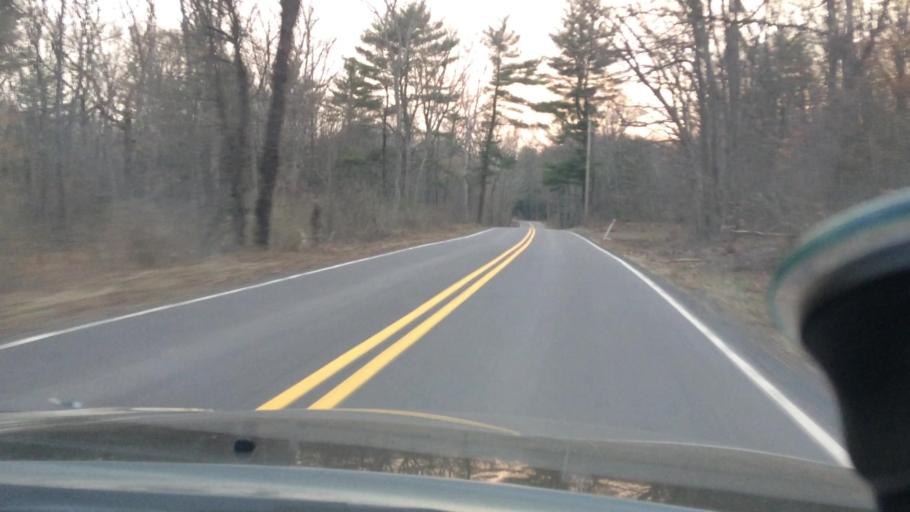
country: US
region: Pennsylvania
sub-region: Luzerne County
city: Freeland
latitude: 41.0769
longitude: -75.9084
